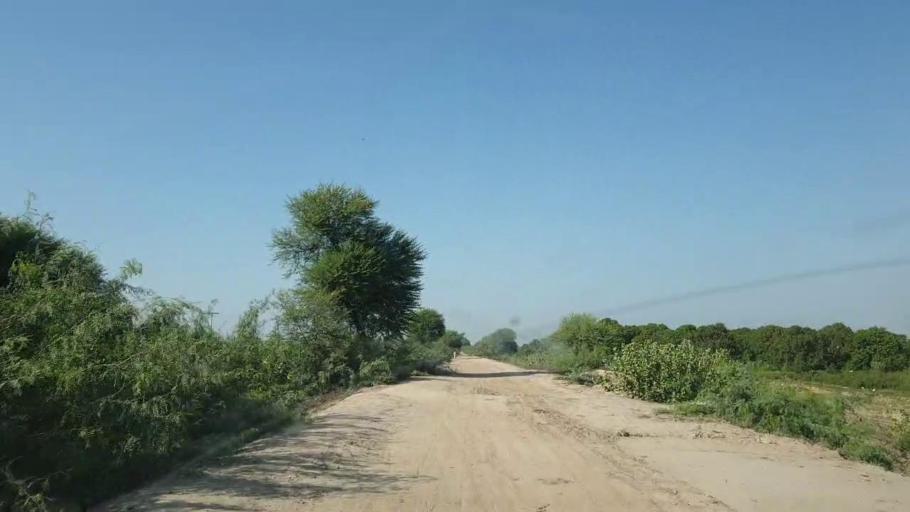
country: PK
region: Sindh
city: Tando Jam
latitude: 25.3658
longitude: 68.5694
